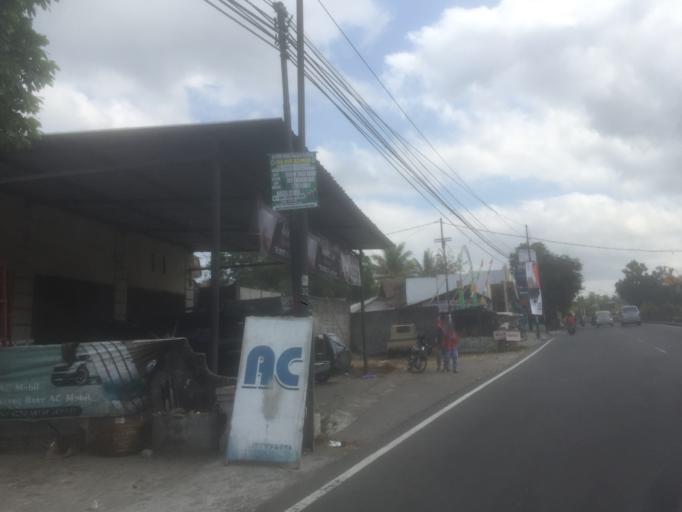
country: ID
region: Daerah Istimewa Yogyakarta
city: Sleman
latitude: -7.6739
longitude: 110.3359
